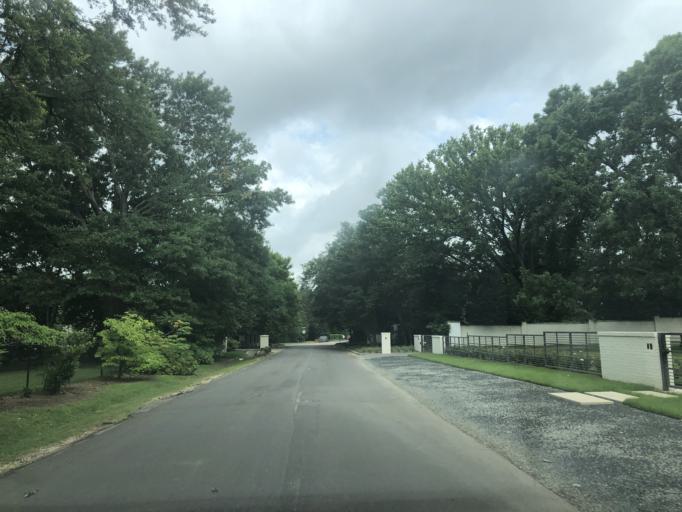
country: US
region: Texas
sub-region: Dallas County
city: University Park
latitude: 32.8687
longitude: -96.8204
